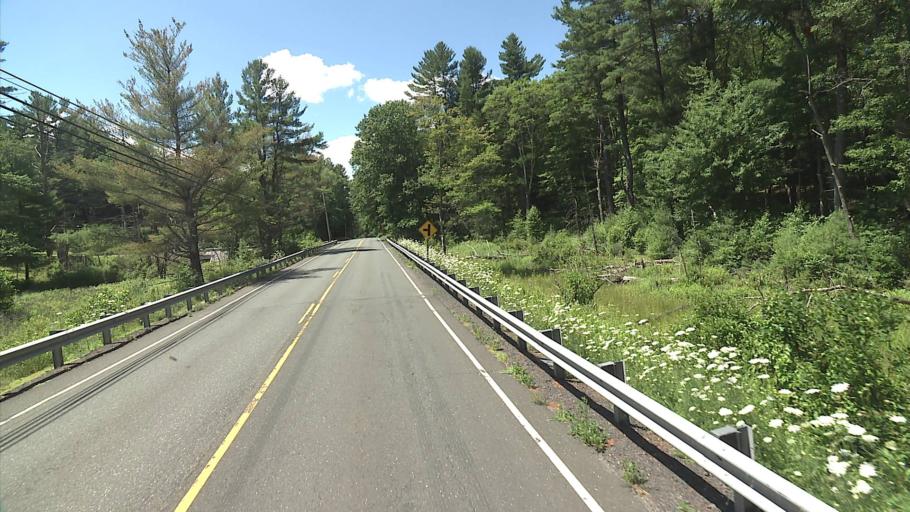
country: US
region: Connecticut
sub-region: Litchfield County
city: New Hartford Center
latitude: 41.9223
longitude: -72.9340
